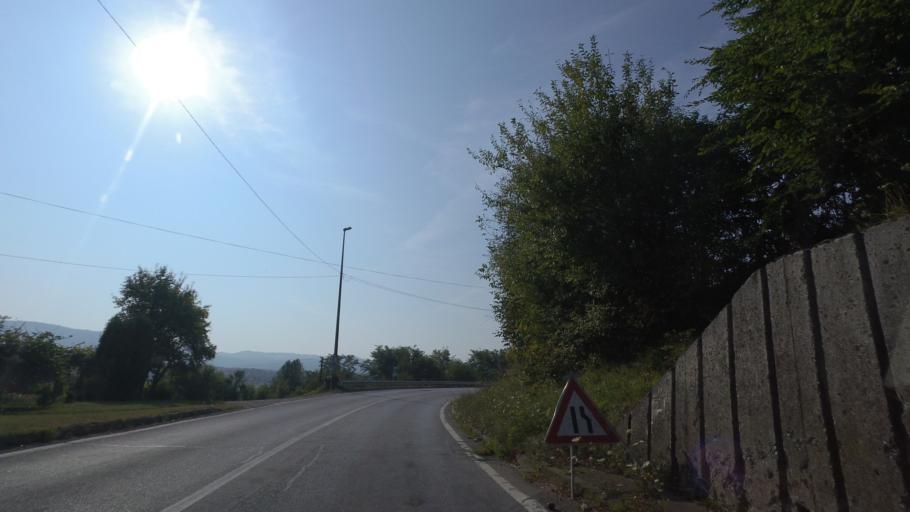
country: HR
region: Pozesko-Slavonska
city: Pakrac
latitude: 45.4276
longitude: 17.1830
